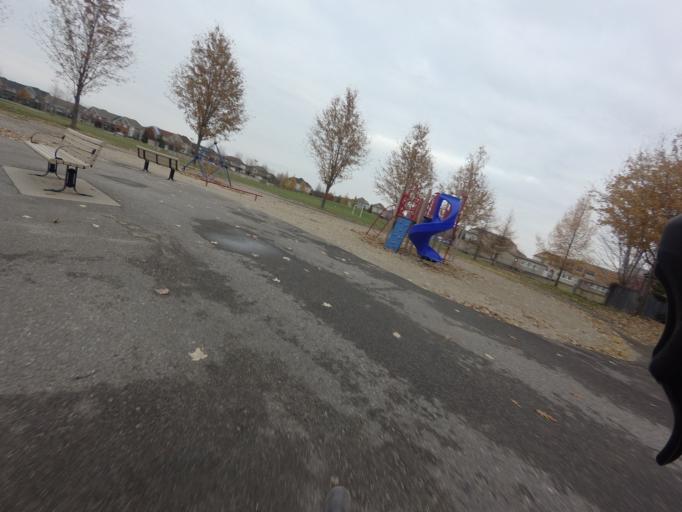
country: CA
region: Ontario
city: Bells Corners
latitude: 45.2832
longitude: -75.7093
